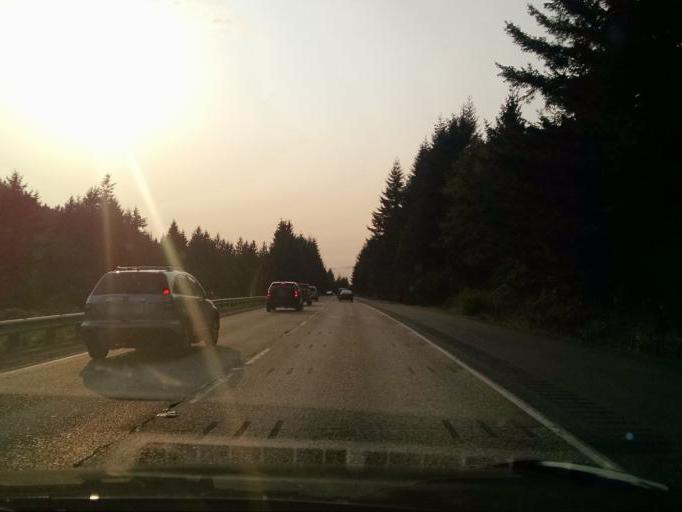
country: US
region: Washington
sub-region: Whatcom County
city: Bellingham
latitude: 48.6981
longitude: -122.4604
